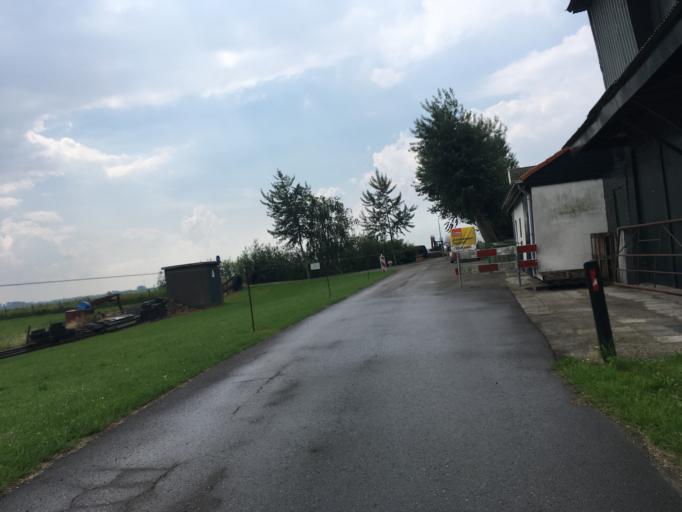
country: NL
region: North Holland
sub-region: Gemeente Haarlem
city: Haarlem
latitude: 52.4054
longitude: 4.7153
